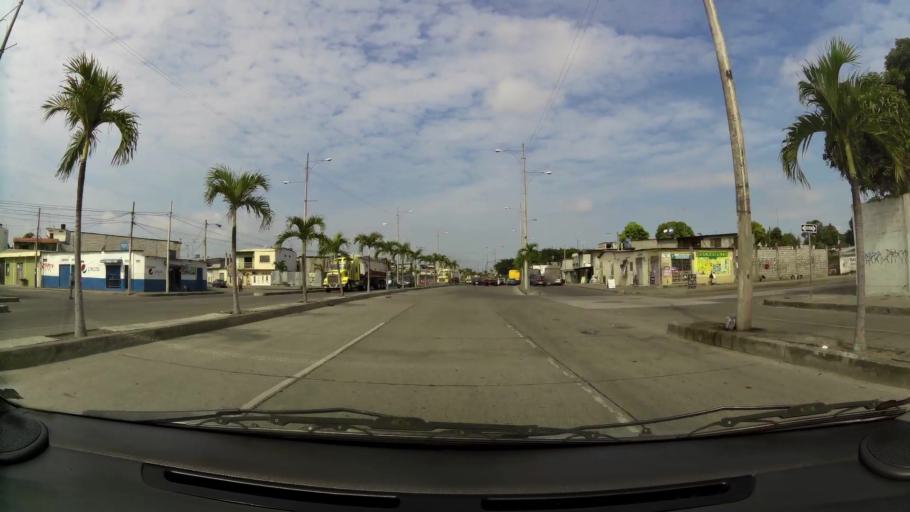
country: EC
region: Guayas
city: Guayaquil
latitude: -2.2607
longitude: -79.8910
